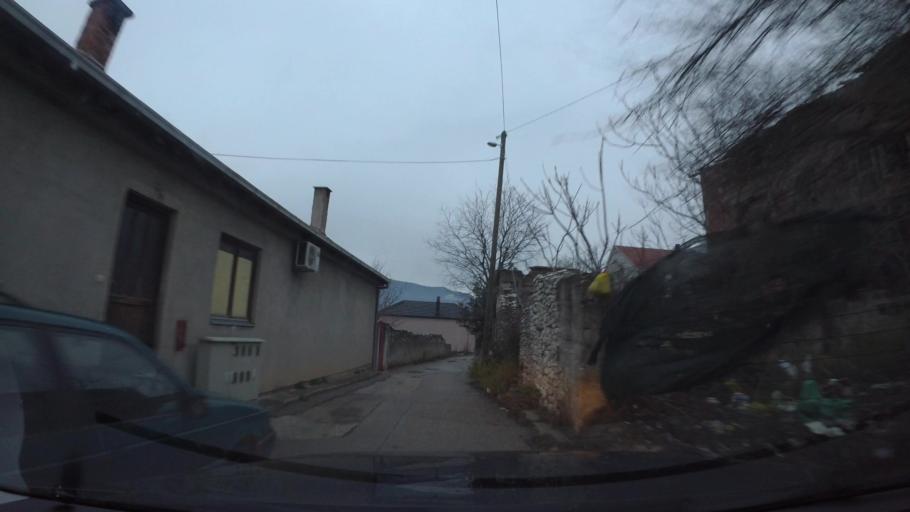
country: BA
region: Federation of Bosnia and Herzegovina
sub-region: Hercegovacko-Bosanski Kanton
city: Mostar
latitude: 43.3280
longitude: 17.8195
